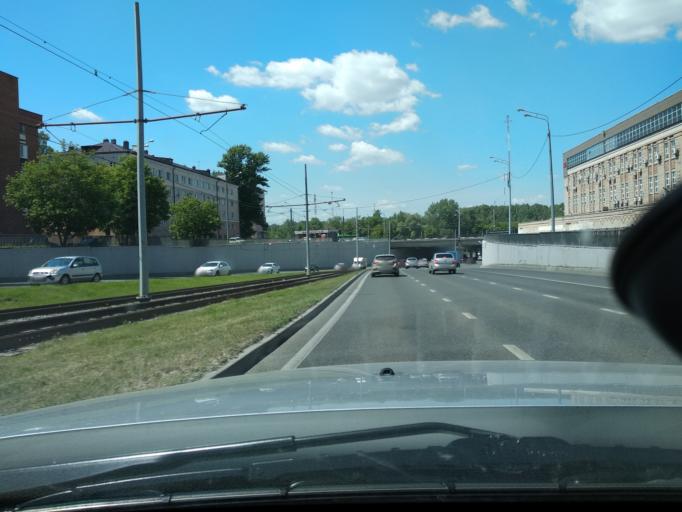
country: RU
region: Tatarstan
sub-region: Gorod Kazan'
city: Kazan
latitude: 55.8151
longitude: 49.1834
